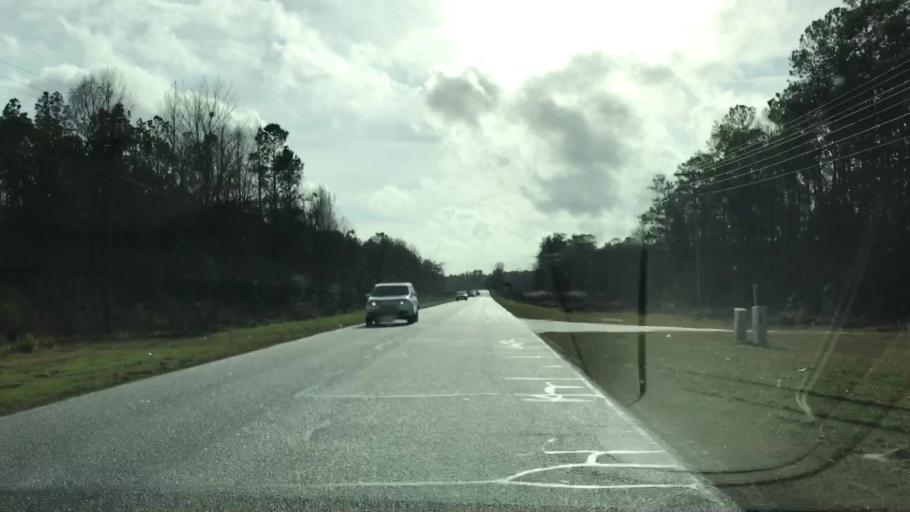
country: US
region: South Carolina
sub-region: Williamsburg County
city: Andrews
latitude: 33.4789
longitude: -79.5561
